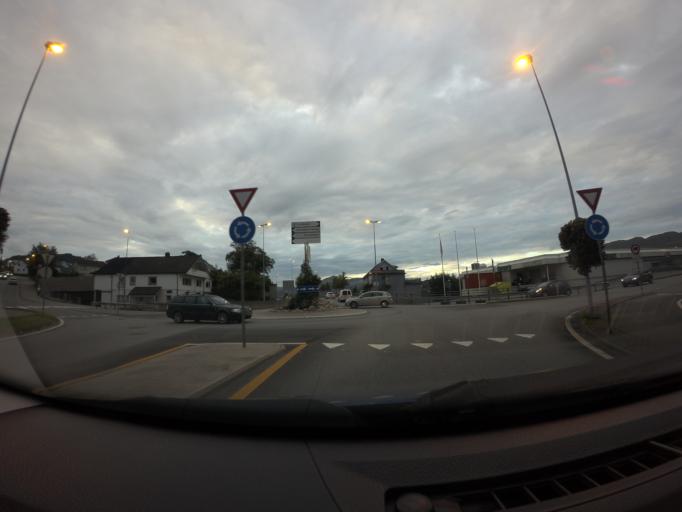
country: NO
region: Rogaland
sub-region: Gjesdal
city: Algard
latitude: 58.7670
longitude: 5.8622
